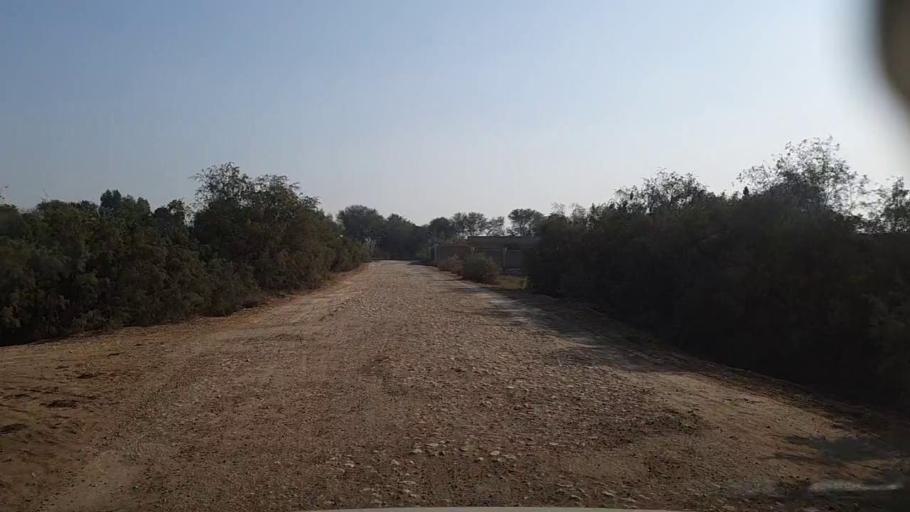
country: PK
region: Sindh
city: Mirpur Mathelo
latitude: 27.8847
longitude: 69.6111
